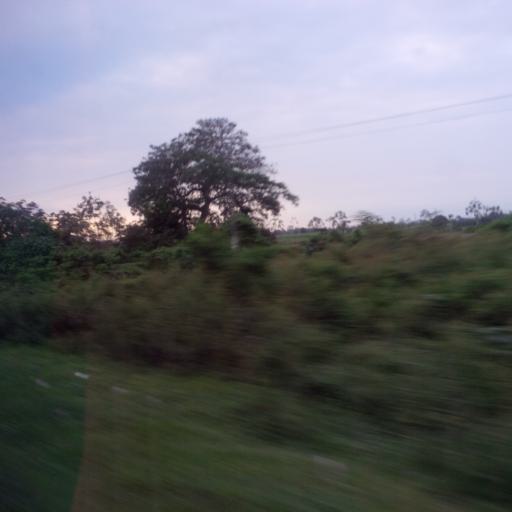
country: EC
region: Guayas
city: Coronel Marcelino Mariduena
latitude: -2.3288
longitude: -79.4183
